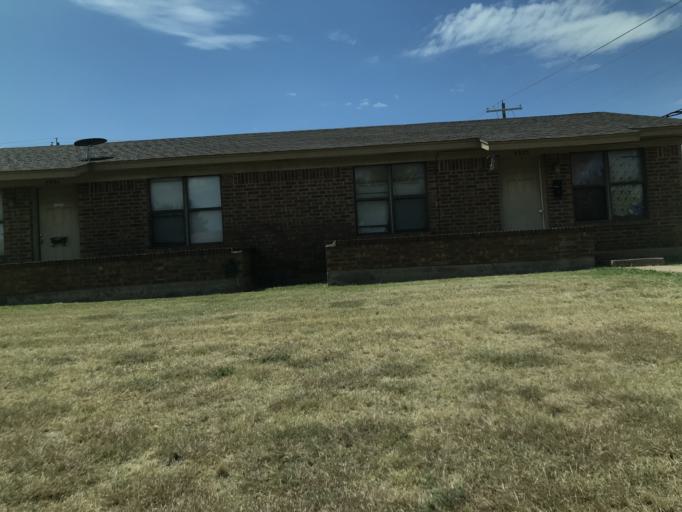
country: US
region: Texas
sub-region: Taylor County
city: Abilene
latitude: 32.4451
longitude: -99.7859
